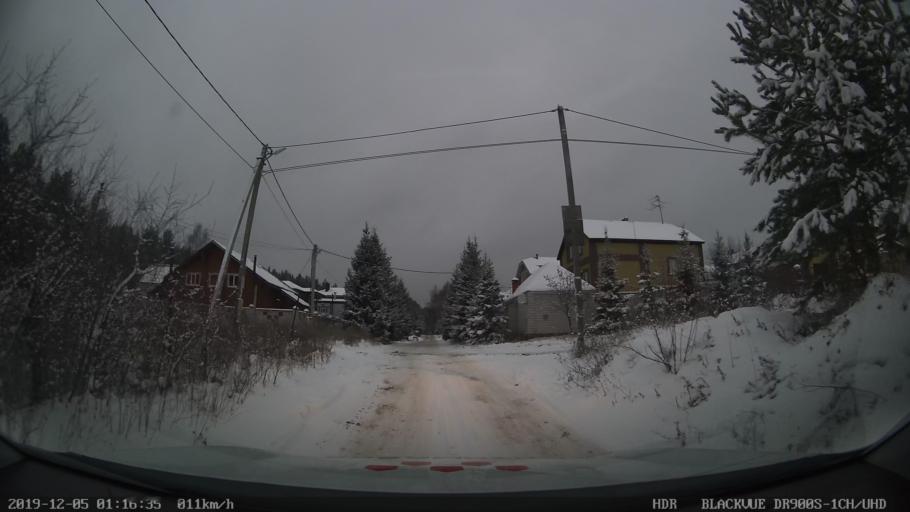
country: RU
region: Tatarstan
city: Stolbishchi
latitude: 55.6471
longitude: 49.1106
